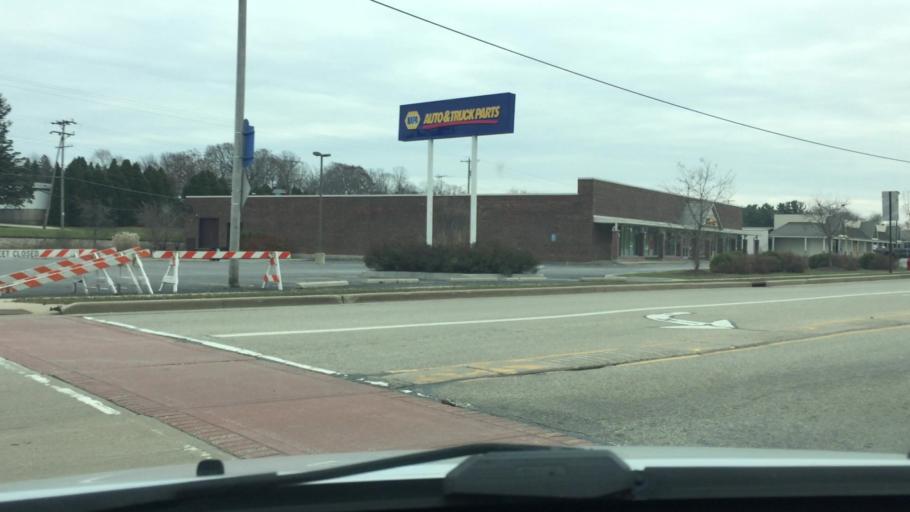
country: US
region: Wisconsin
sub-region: Ozaukee County
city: Grafton
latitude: 43.3117
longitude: -87.9568
